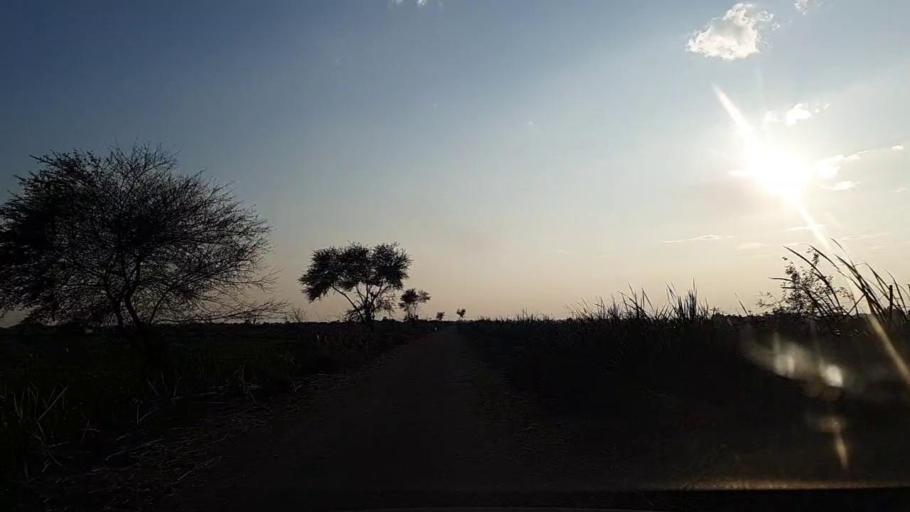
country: PK
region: Sindh
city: Sanghar
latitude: 26.2623
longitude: 68.9791
